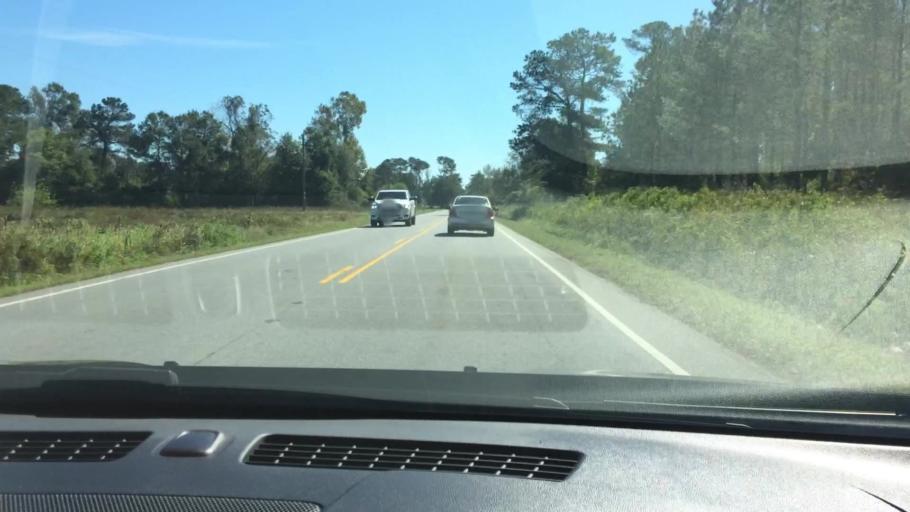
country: US
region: North Carolina
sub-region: Pitt County
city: Grifton
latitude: 35.3478
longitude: -77.3237
